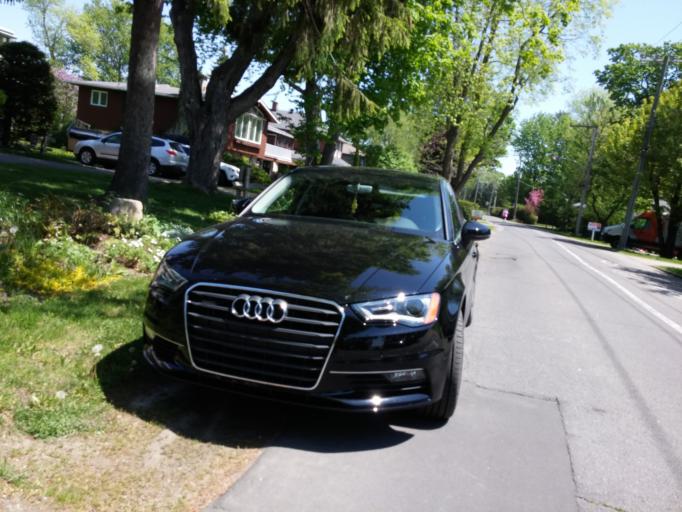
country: CA
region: Quebec
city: Baie-D'Urfe
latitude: 45.4148
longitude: -73.8942
